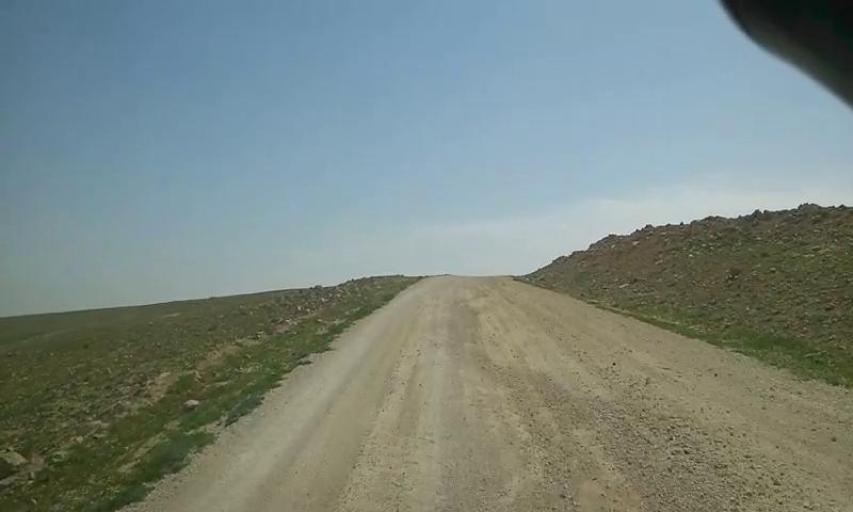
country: PS
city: `Arab ar Rashaydah
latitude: 31.5203
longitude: 35.2969
